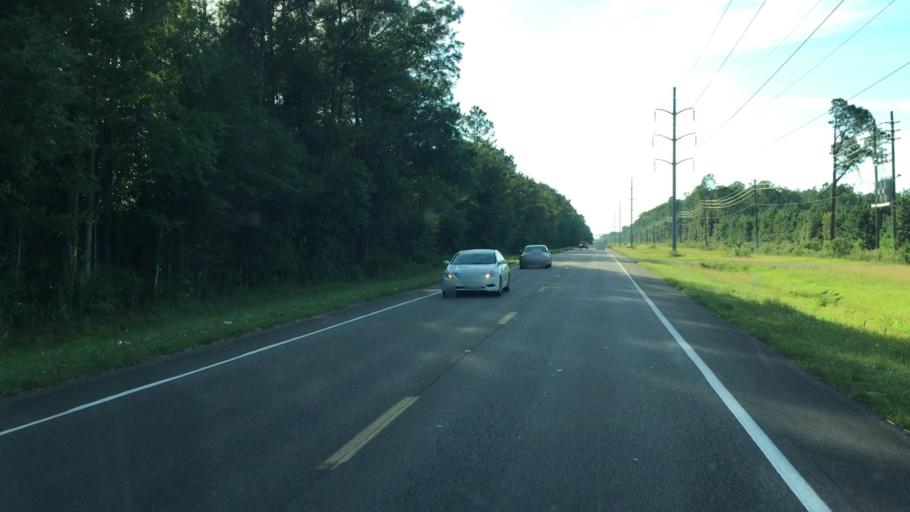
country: US
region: Florida
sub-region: Alachua County
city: Gainesville
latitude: 29.7030
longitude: -82.3107
